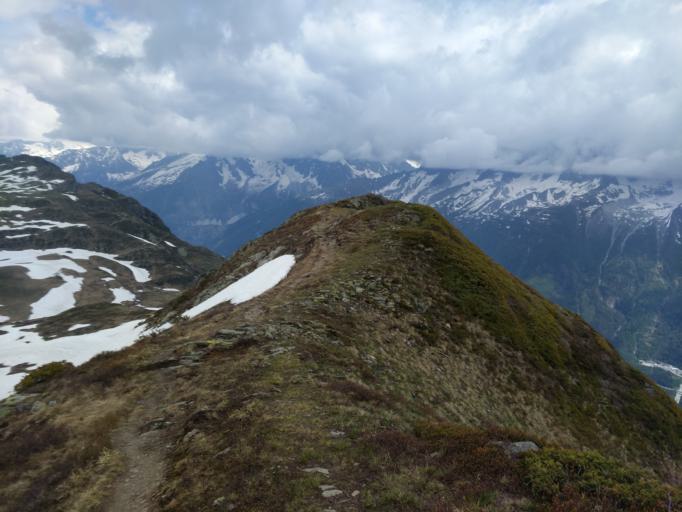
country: FR
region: Rhone-Alpes
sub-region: Departement de la Haute-Savoie
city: Les Houches
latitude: 45.9197
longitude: 6.8165
